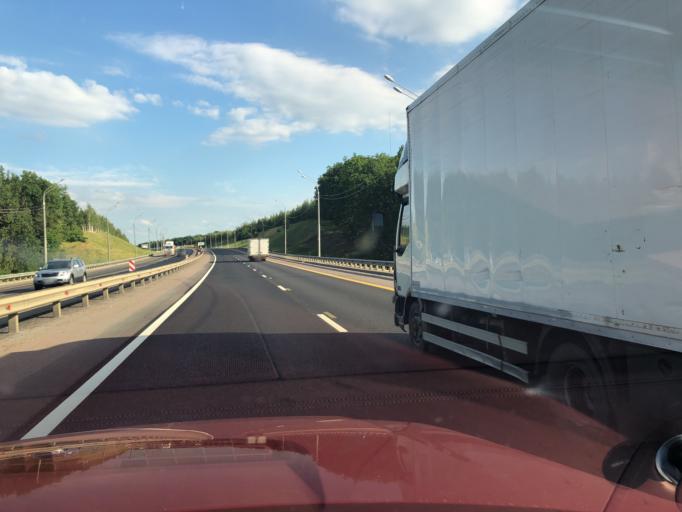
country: RU
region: Lipetsk
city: Zadonsk
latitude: 52.3925
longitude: 38.8631
